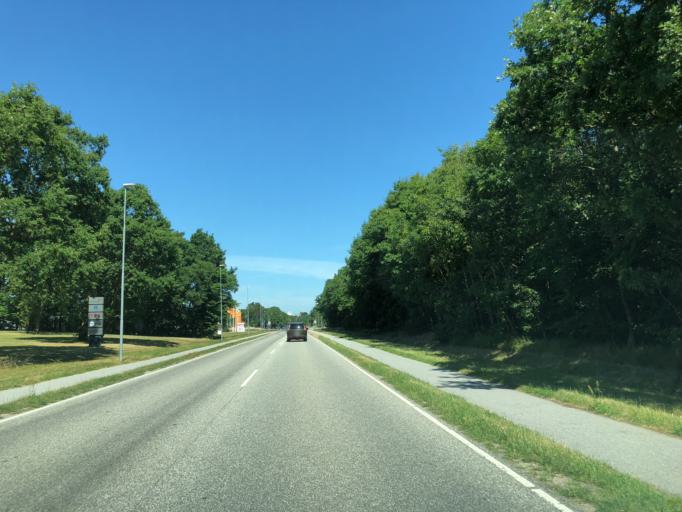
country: DK
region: Central Jutland
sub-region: Skive Kommune
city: Skive
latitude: 56.5511
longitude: 9.0254
